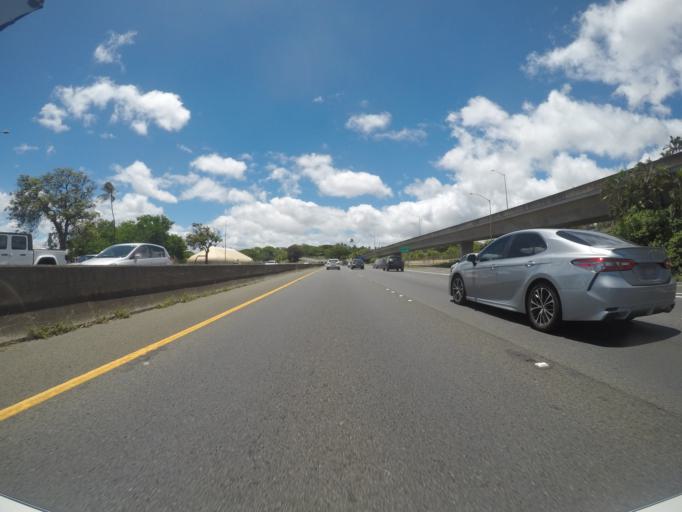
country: US
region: Hawaii
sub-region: Honolulu County
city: Honolulu
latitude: 21.3402
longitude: -157.8854
